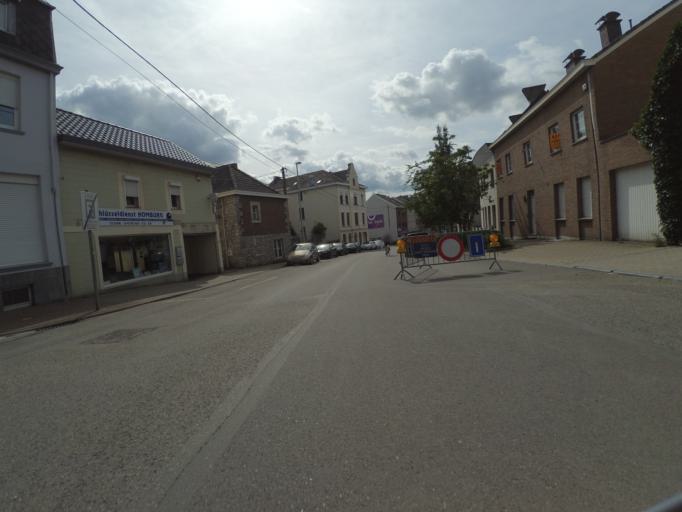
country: BE
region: Wallonia
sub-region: Province de Liege
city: Eupen
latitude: 50.6339
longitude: 6.0373
